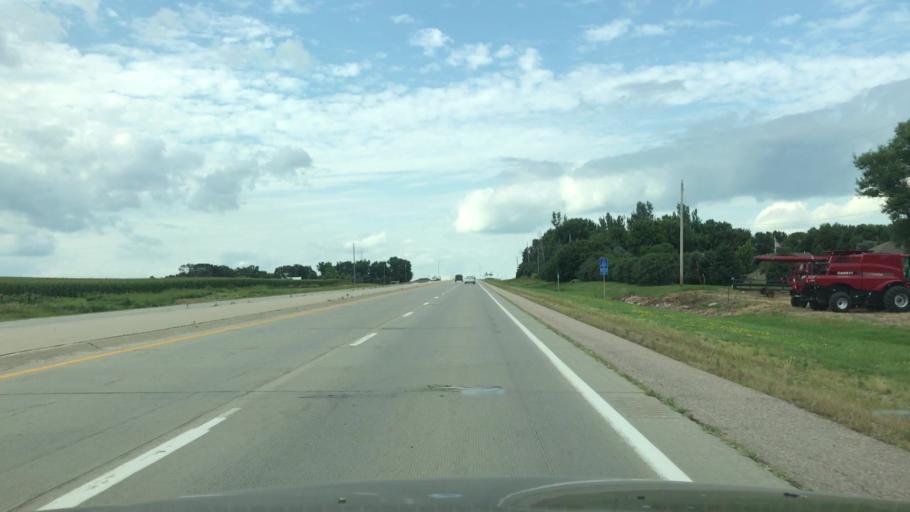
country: US
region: Iowa
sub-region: Plymouth County
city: Le Mars
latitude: 42.8106
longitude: -96.1747
